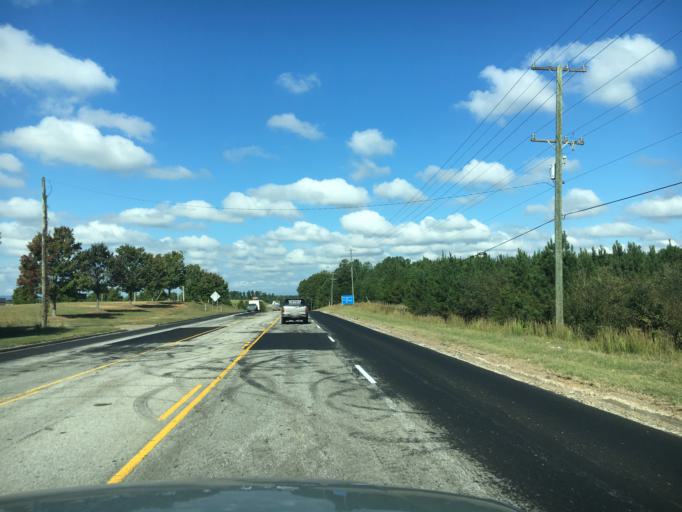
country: US
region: South Carolina
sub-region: Greenville County
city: Greer
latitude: 34.9076
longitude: -82.1996
